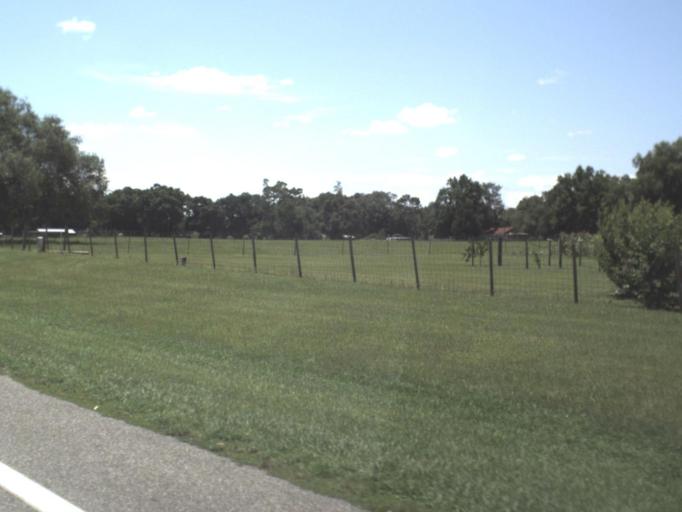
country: US
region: Florida
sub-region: Lafayette County
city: Mayo
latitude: 30.0533
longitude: -83.1089
